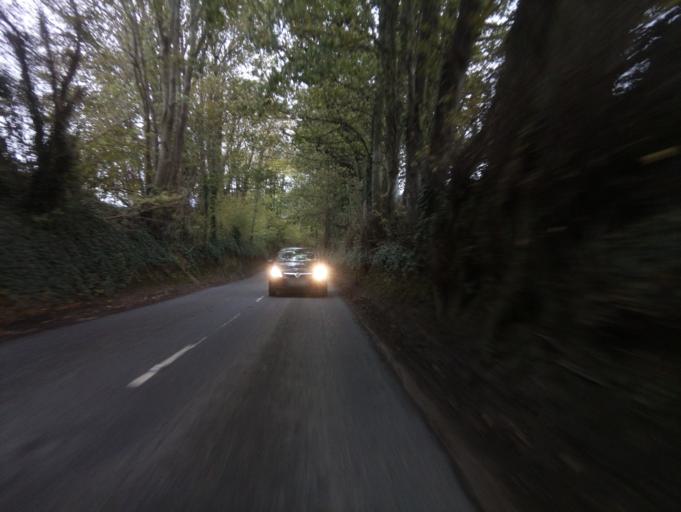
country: GB
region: England
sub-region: Dorset
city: Sherborne
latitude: 50.9820
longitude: -2.5658
